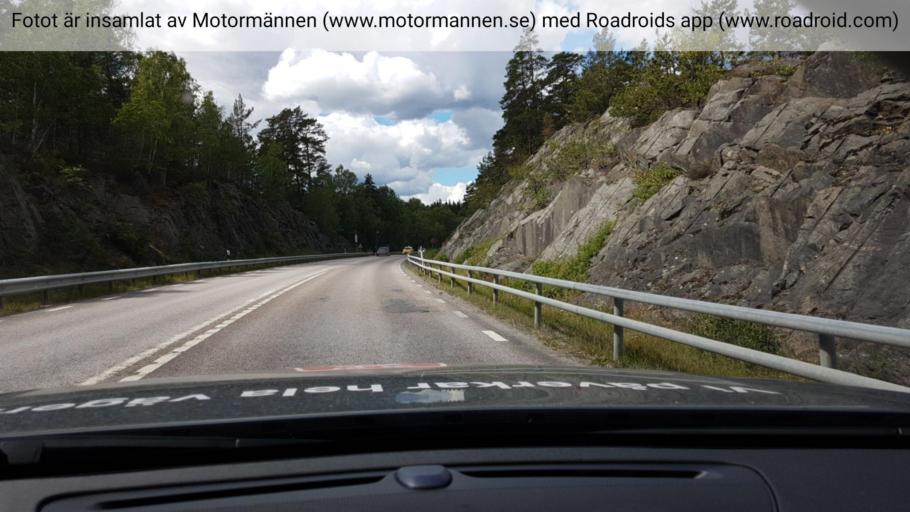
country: SE
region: Stockholm
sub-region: Lidingo
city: Brevik
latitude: 59.4282
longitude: 18.2260
